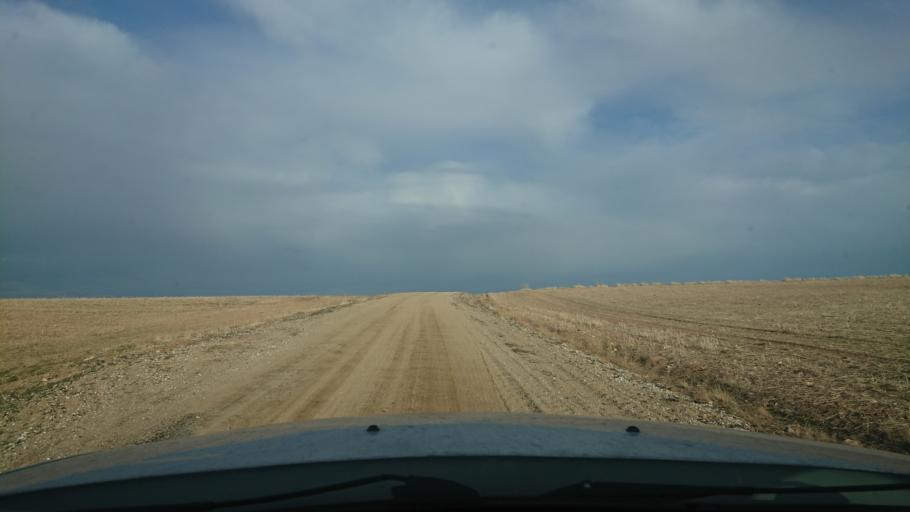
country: TR
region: Aksaray
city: Ortakoy
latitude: 38.7029
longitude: 33.8730
